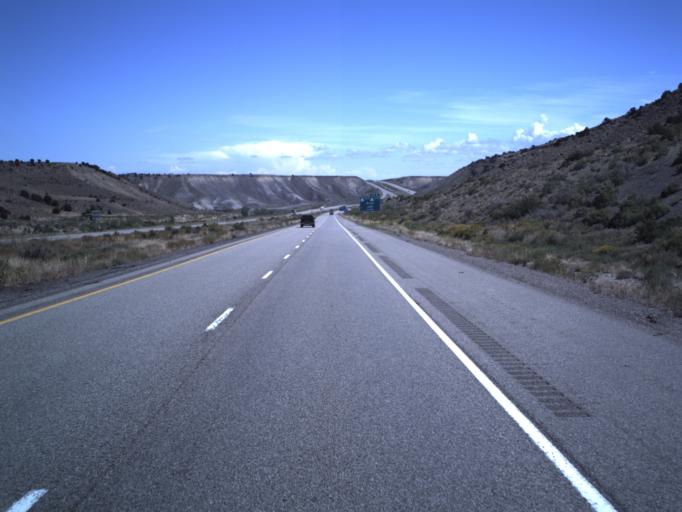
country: US
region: Utah
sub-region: Emery County
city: Ferron
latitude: 38.7613
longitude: -111.3661
